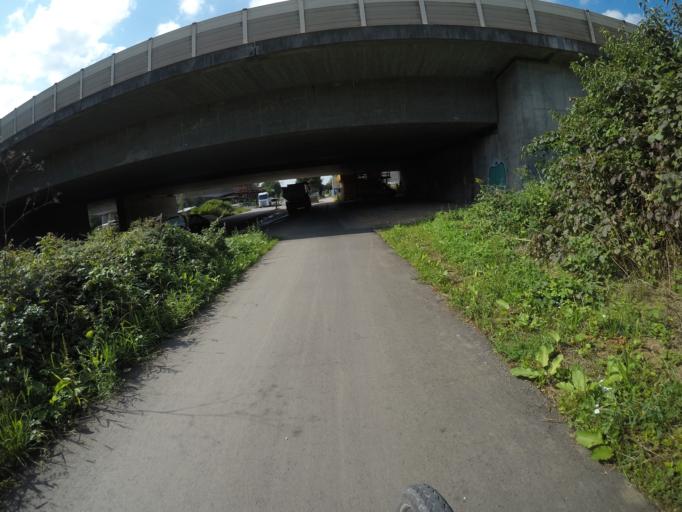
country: DE
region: Baden-Wuerttemberg
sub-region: Regierungsbezirk Stuttgart
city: Wendlingen am Neckar
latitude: 48.6675
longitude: 9.3643
